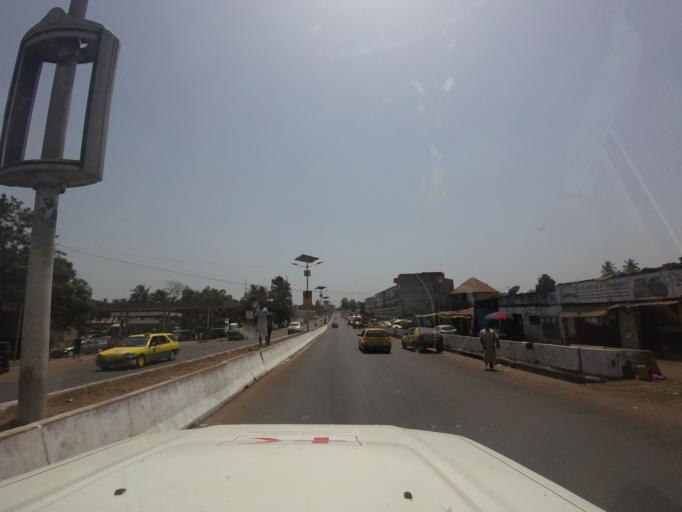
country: GN
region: Conakry
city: Conakry
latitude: 9.5635
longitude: -13.6388
